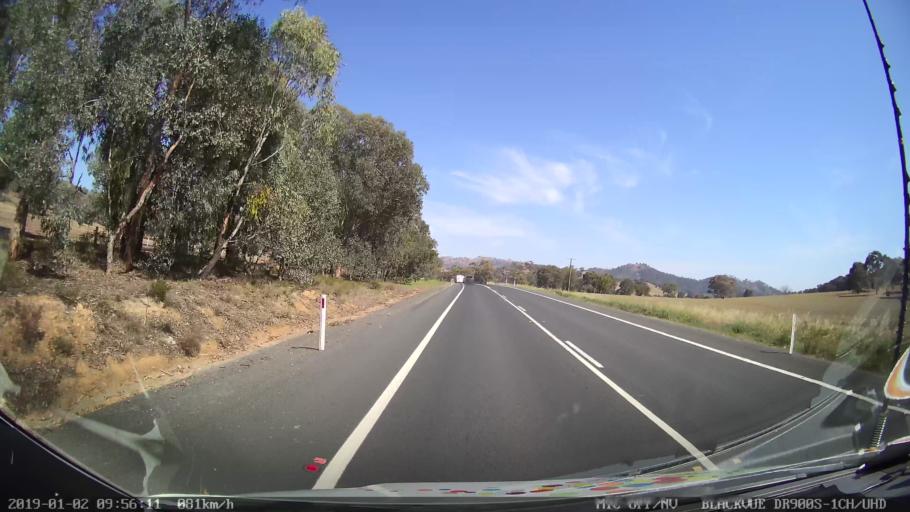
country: AU
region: New South Wales
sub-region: Tumut Shire
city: Tumut
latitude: -35.2173
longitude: 148.1792
